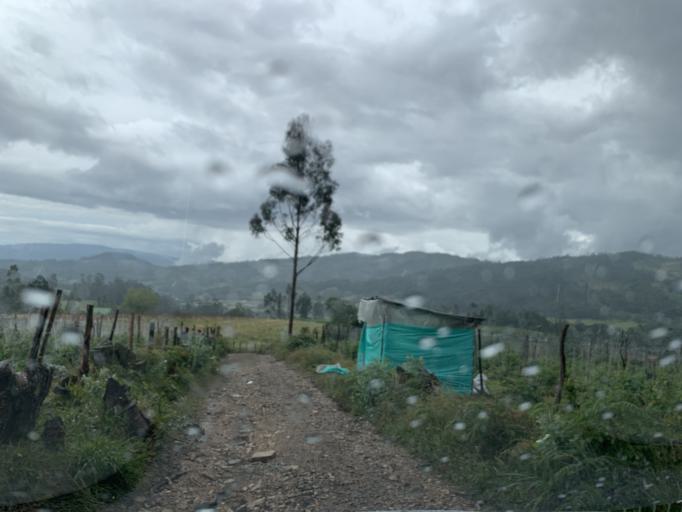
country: CO
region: Boyaca
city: Arcabuco
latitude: 5.7516
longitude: -73.4711
